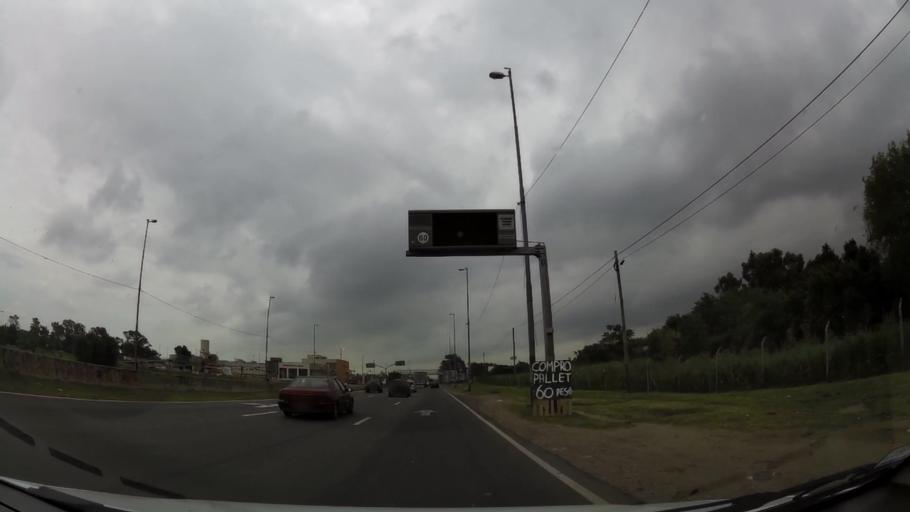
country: AR
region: Buenos Aires
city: San Justo
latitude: -34.7083
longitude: -58.5303
